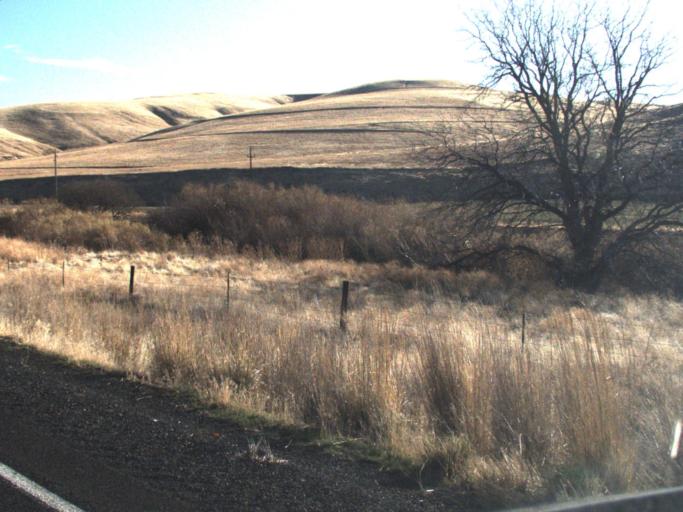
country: US
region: Washington
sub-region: Garfield County
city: Pomeroy
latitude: 46.4635
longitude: -117.6844
